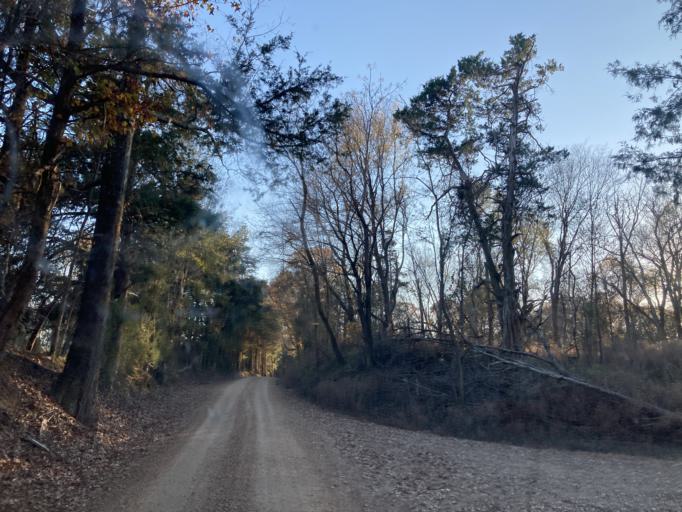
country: US
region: Mississippi
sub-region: Yazoo County
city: Yazoo City
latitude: 32.9453
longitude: -90.2855
